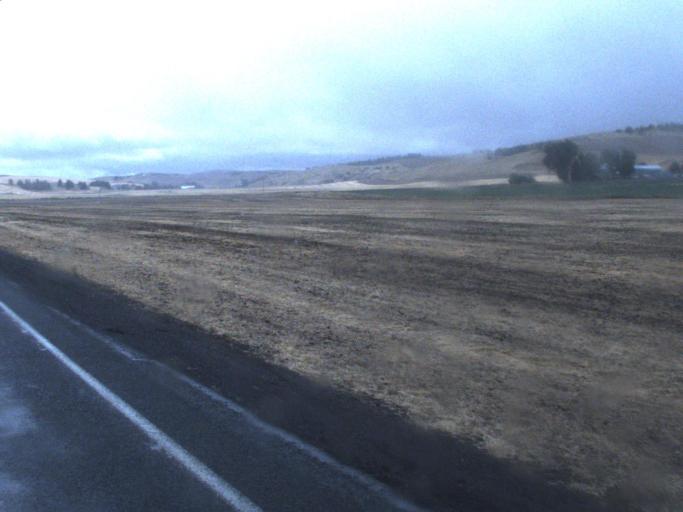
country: US
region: Washington
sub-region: Whitman County
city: Colfax
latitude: 47.0686
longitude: -117.5309
